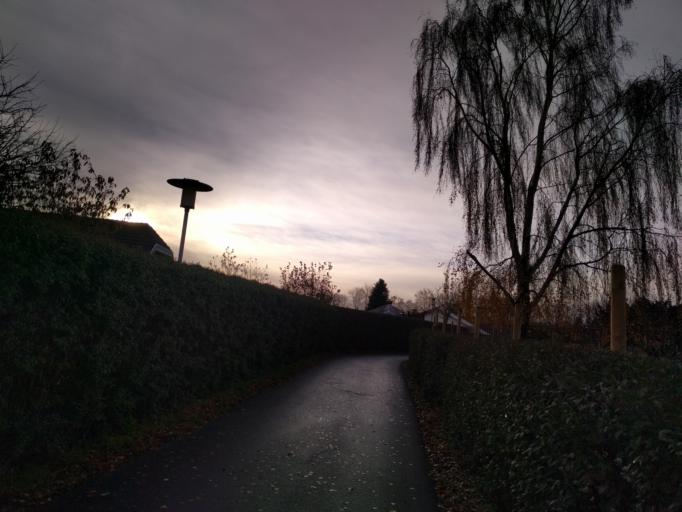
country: DK
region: South Denmark
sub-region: Fredericia Kommune
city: Snoghoj
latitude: 55.5355
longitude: 9.7255
